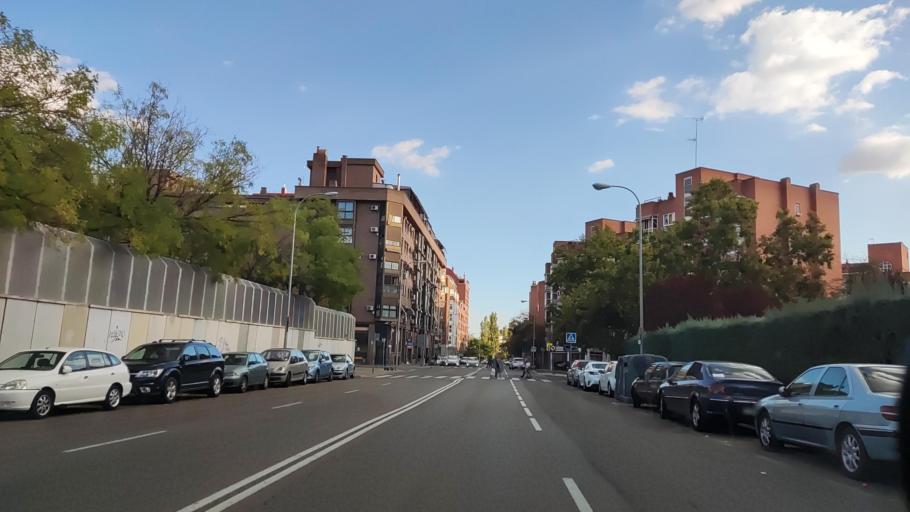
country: ES
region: Madrid
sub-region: Provincia de Madrid
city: Arganzuela
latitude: 40.3991
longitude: -3.7054
